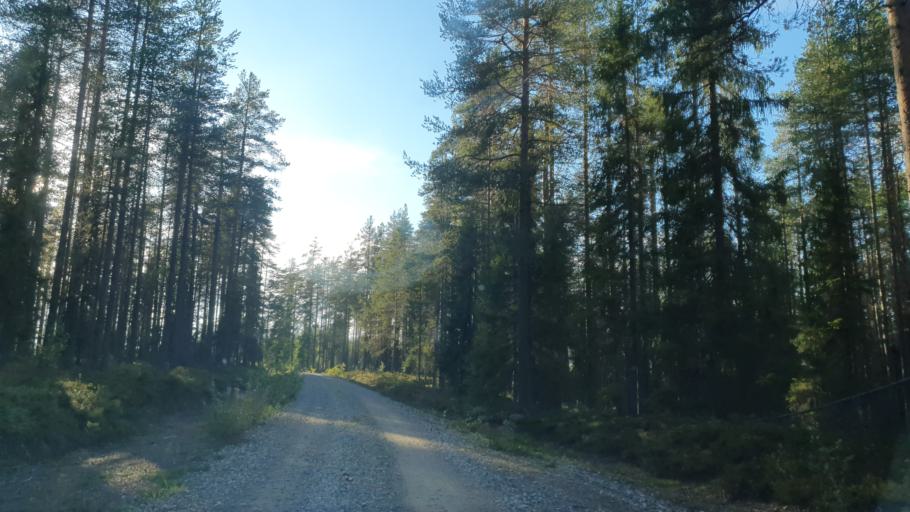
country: FI
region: Kainuu
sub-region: Kehys-Kainuu
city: Kuhmo
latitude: 64.3300
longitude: 30.0231
